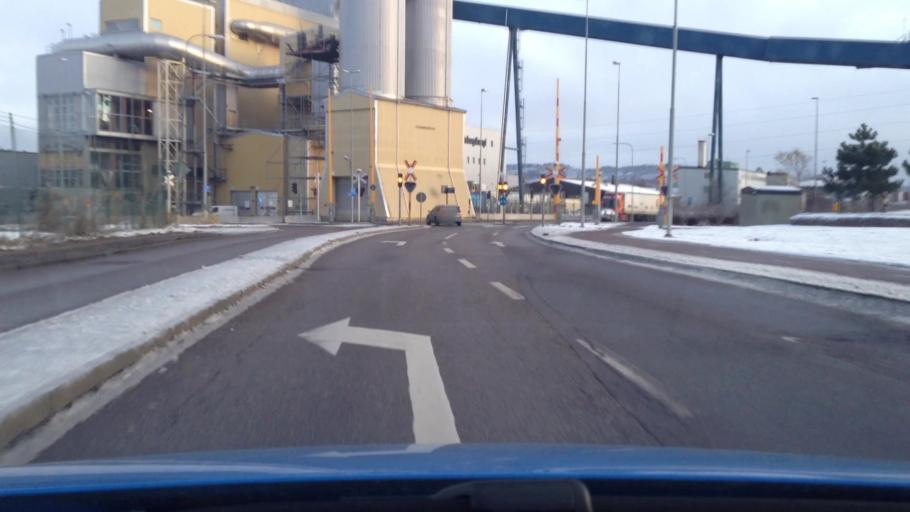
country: SE
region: Vaestra Goetaland
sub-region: Goteborg
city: Eriksbo
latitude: 57.7288
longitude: 12.0340
